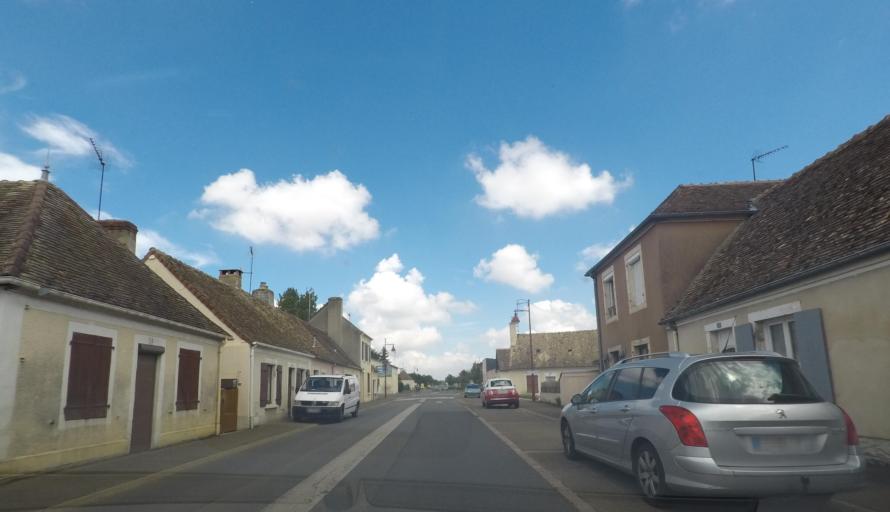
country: FR
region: Pays de la Loire
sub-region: Departement de la Sarthe
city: Bonnetable
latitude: 48.2276
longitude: 0.4304
